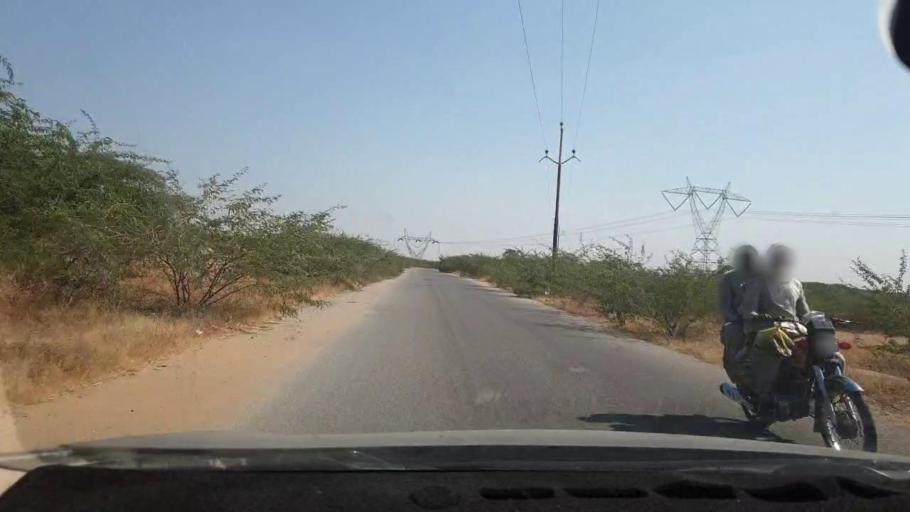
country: PK
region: Sindh
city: Malir Cantonment
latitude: 25.1442
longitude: 67.1900
